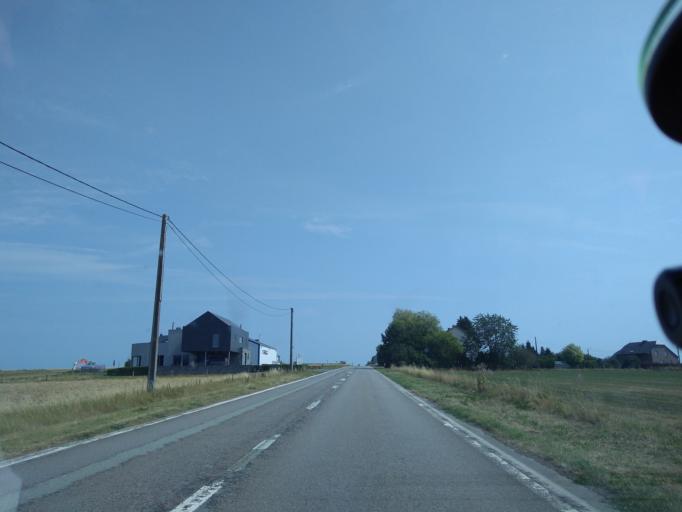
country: BE
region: Wallonia
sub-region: Province du Luxembourg
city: Tenneville
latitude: 50.1529
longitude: 5.5212
